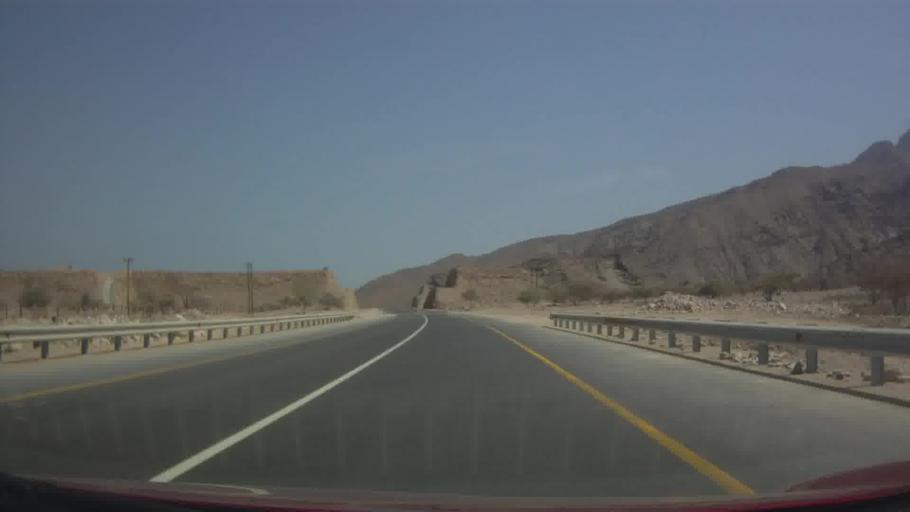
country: OM
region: Muhafazat Masqat
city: Muscat
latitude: 23.3954
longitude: 58.7856
